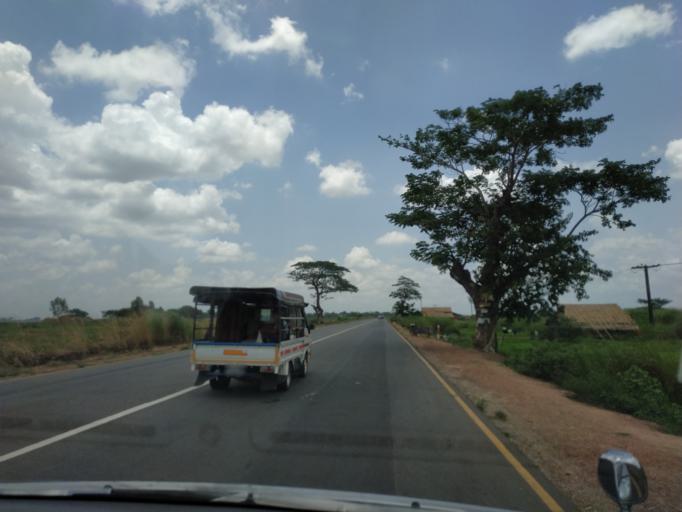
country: MM
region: Bago
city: Bago
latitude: 17.4689
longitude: 96.5668
